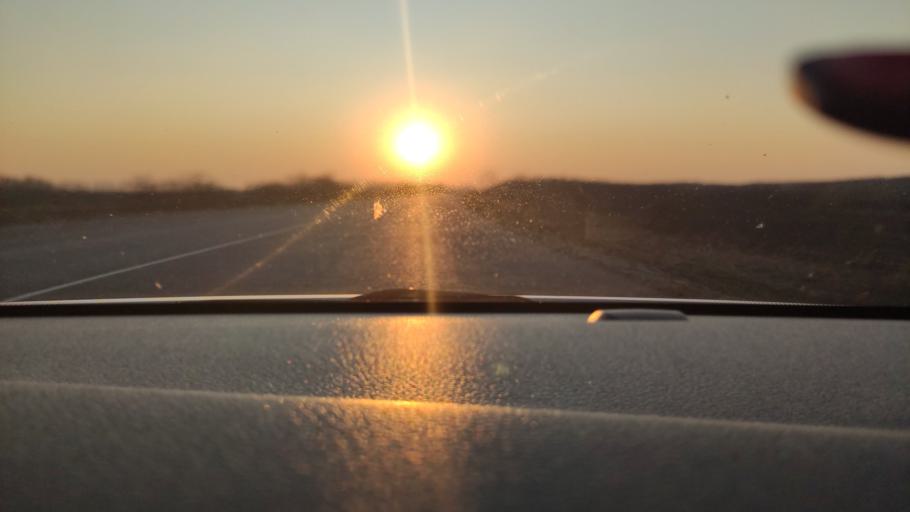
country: RU
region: Voronezj
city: Kolodeznyy
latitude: 51.3391
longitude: 39.0541
